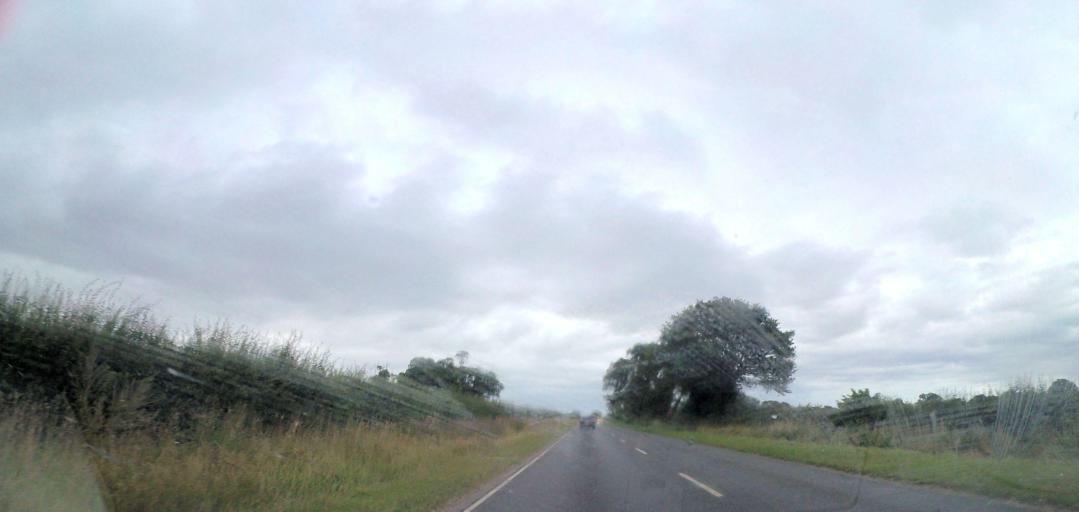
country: GB
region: England
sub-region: Norfolk
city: Coltishall
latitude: 52.7062
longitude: 1.3456
